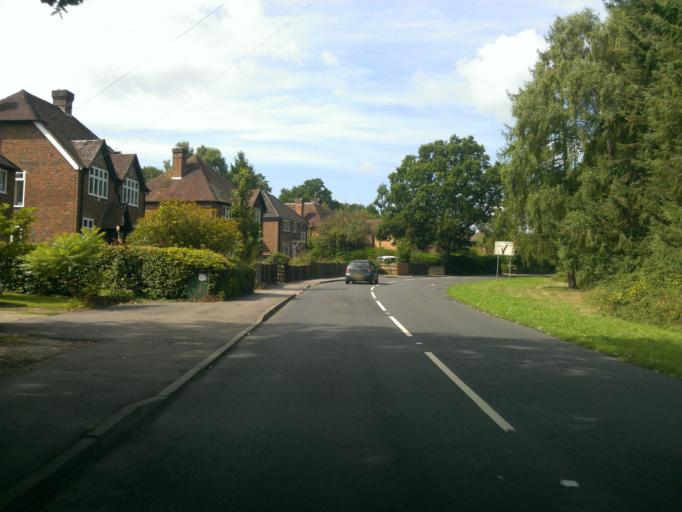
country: GB
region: England
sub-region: Kent
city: Tonbridge
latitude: 51.1957
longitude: 0.2039
